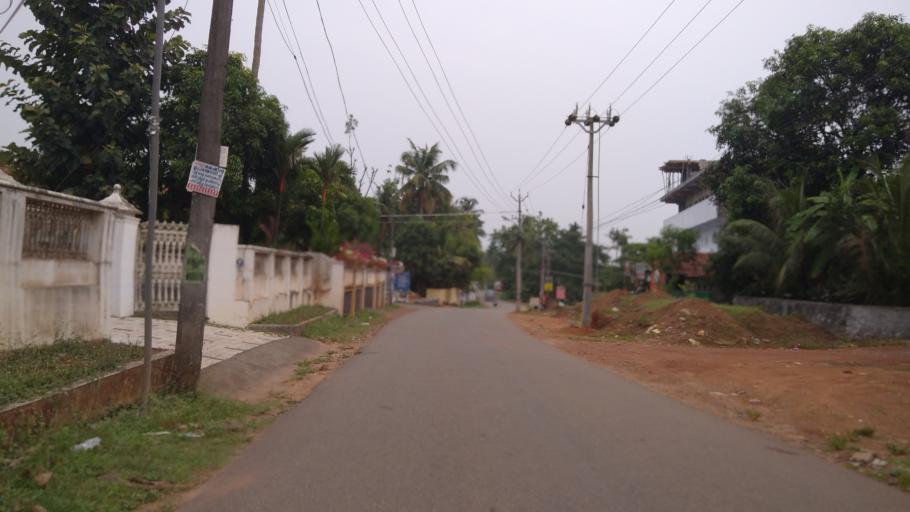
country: IN
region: Kerala
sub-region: Ernakulam
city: Angamali
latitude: 10.1763
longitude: 76.3985
